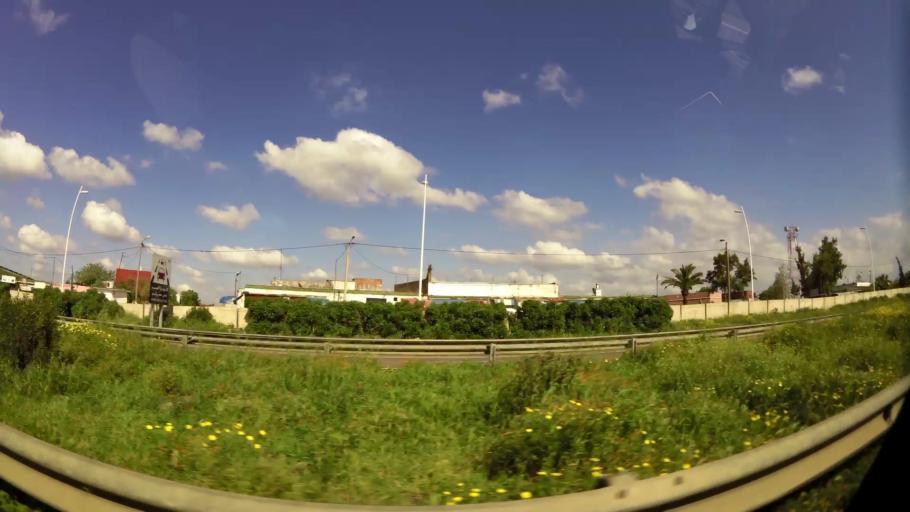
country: MA
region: Chaouia-Ouardigha
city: Nouaseur
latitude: 33.3802
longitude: -7.6219
